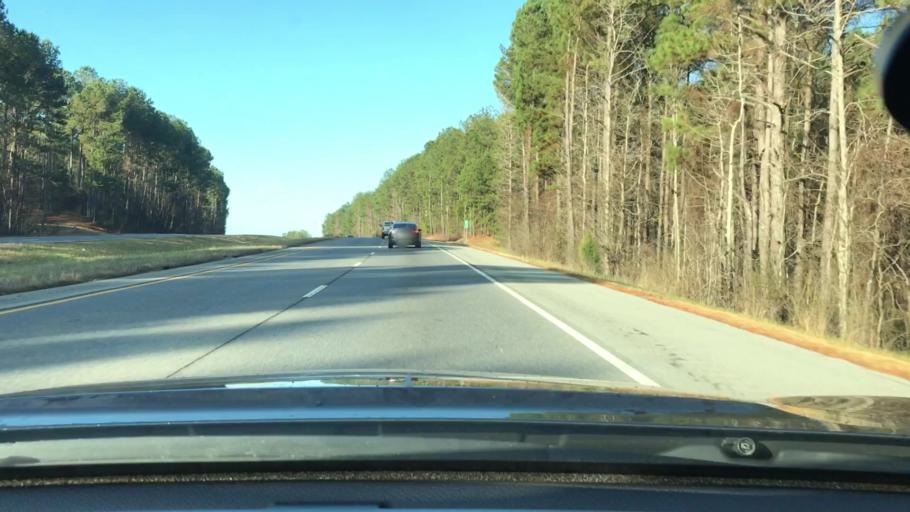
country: US
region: Alabama
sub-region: Shelby County
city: Westover
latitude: 33.3578
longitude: -86.5065
